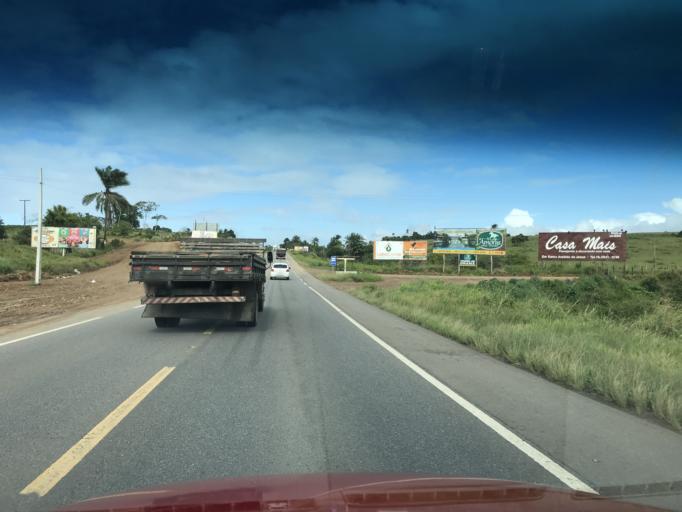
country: BR
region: Bahia
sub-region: Conceicao Do Almeida
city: Muritiba
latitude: -12.9152
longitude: -39.2437
